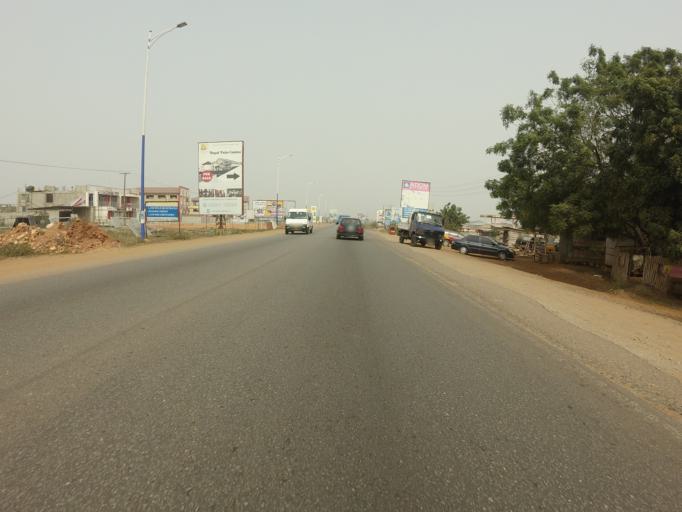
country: GH
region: Greater Accra
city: Tema
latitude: 5.7424
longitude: 0.0365
